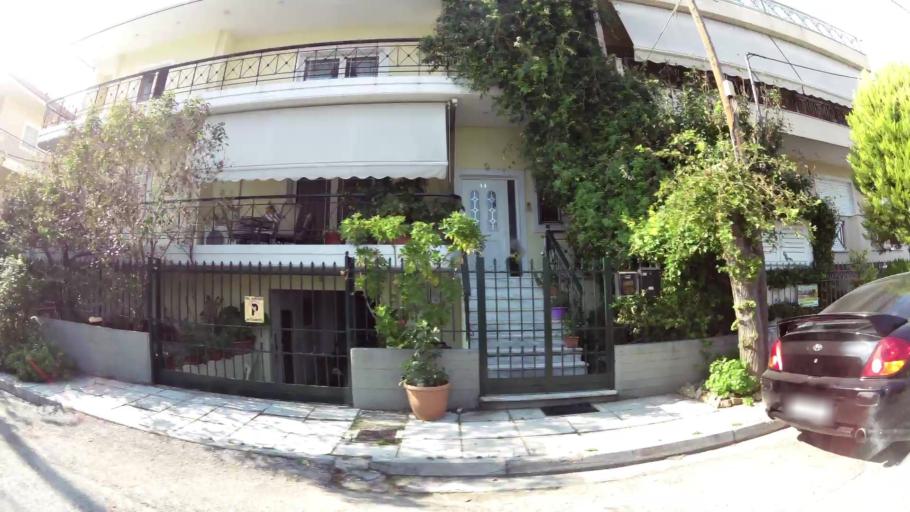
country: GR
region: Attica
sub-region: Nomarchia Athinas
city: Kamateron
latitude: 38.0510
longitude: 23.7110
